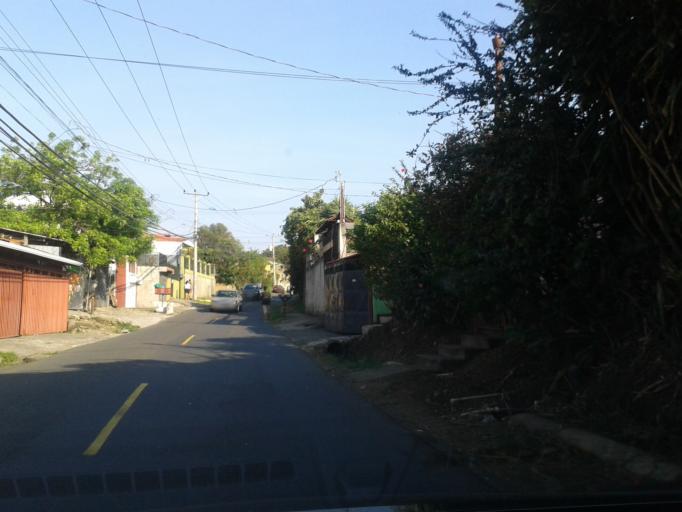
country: CR
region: Heredia
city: Mercedes
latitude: 10.0068
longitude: -84.1433
